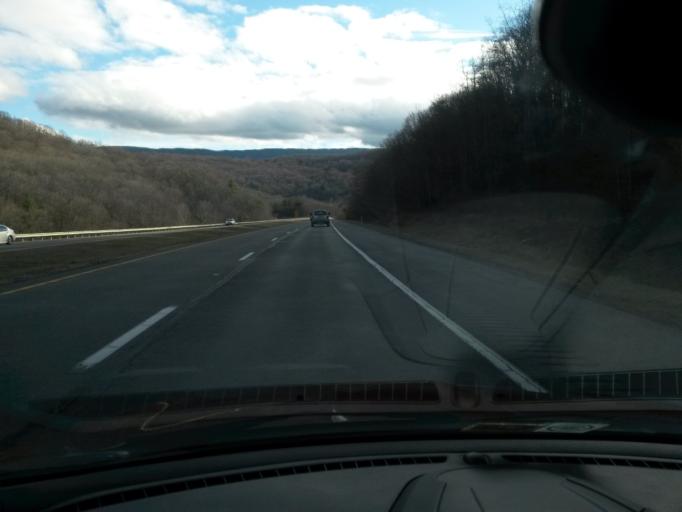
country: US
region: West Virginia
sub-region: Mercer County
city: Athens
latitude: 37.3477
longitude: -81.0137
